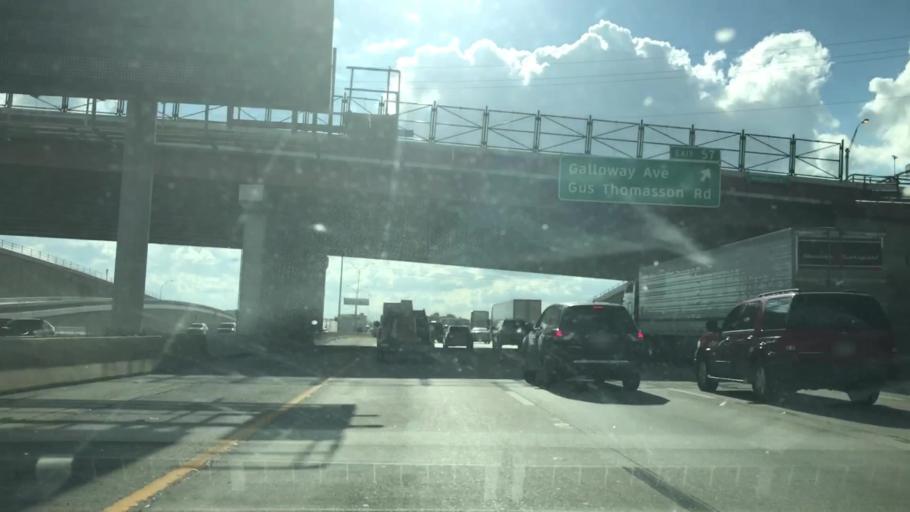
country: US
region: Texas
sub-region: Dallas County
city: Sunnyvale
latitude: 32.8333
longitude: -96.6123
